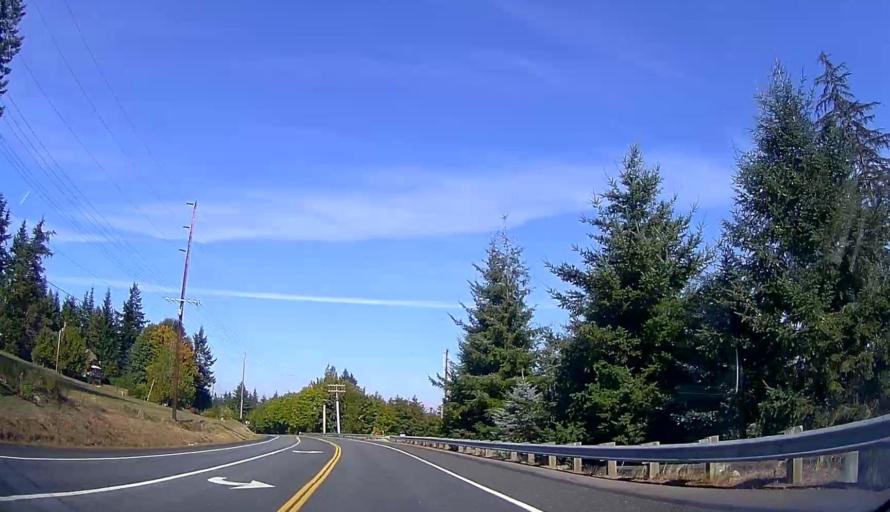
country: US
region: Washington
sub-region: Island County
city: Camano
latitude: 48.1956
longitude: -122.4857
